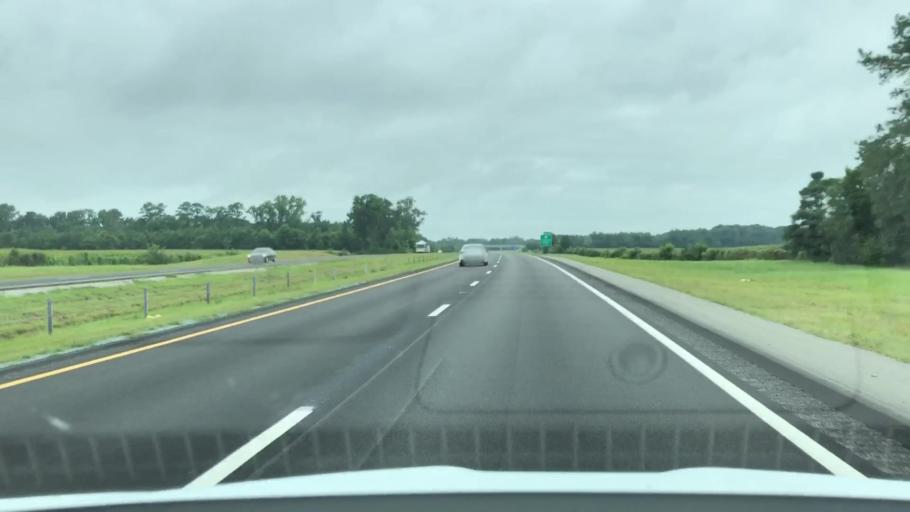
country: US
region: North Carolina
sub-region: Wayne County
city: Fremont
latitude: 35.5292
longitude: -77.9888
